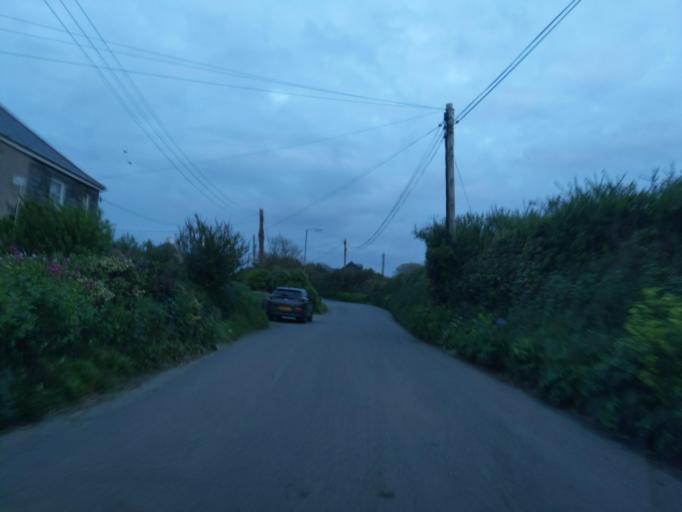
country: GB
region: England
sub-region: Cornwall
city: Polzeath
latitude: 50.5592
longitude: -4.8784
